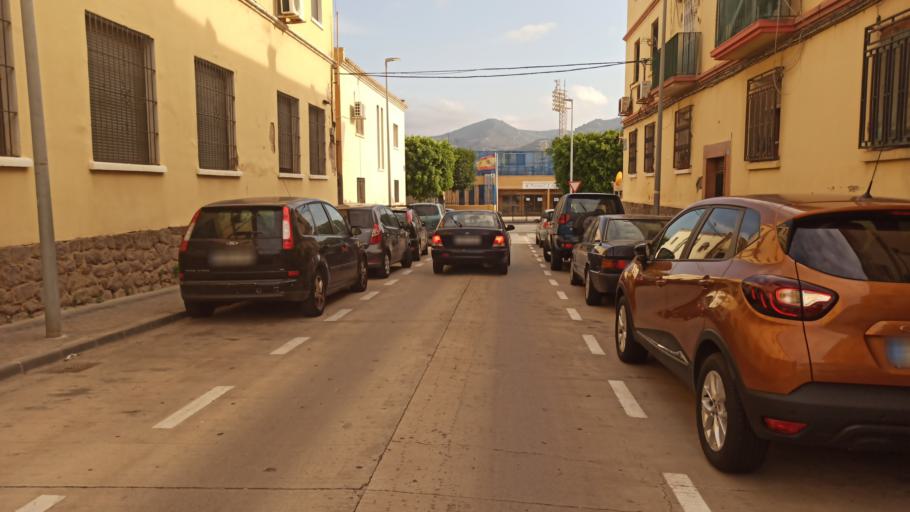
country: ES
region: Melilla
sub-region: Melilla
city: Melilla
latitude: 35.2867
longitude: -2.9496
